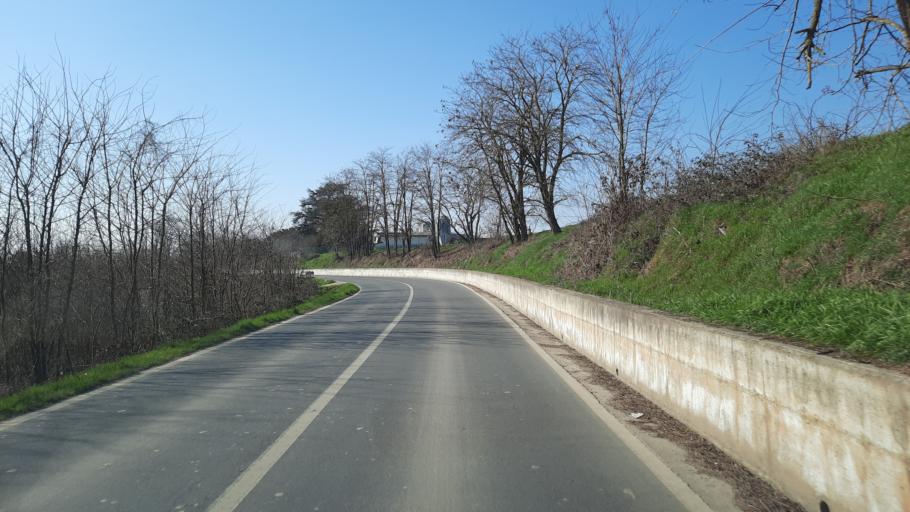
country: IT
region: Piedmont
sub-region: Provincia di Vercelli
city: Trino
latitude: 45.2054
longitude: 8.3145
